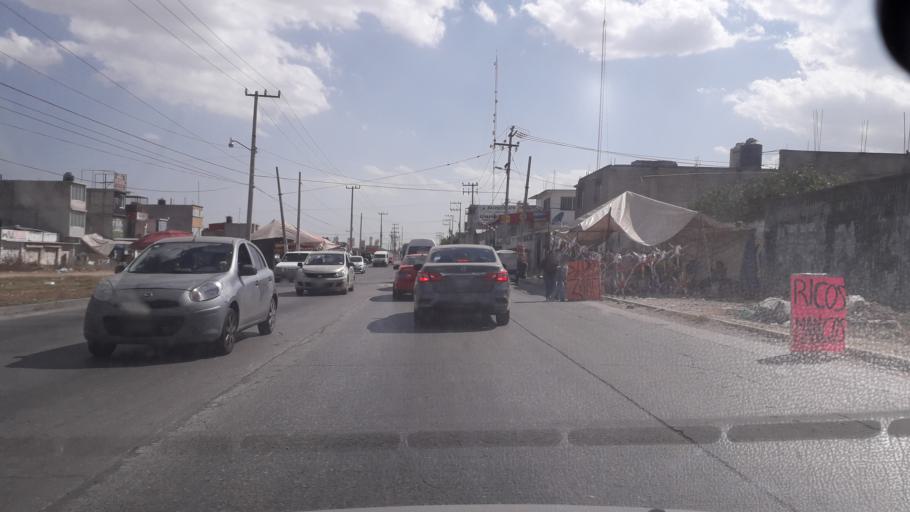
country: MX
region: Mexico
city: Ecatepec
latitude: 19.6262
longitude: -99.0495
